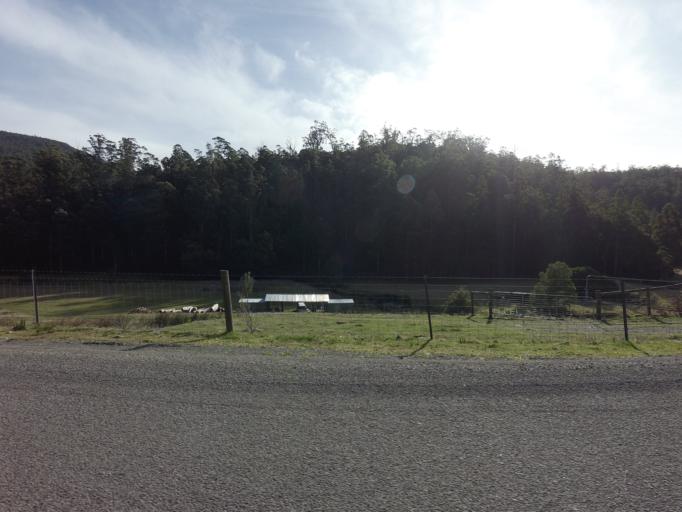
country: AU
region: Tasmania
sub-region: Huon Valley
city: Huonville
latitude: -43.0437
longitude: 147.1227
